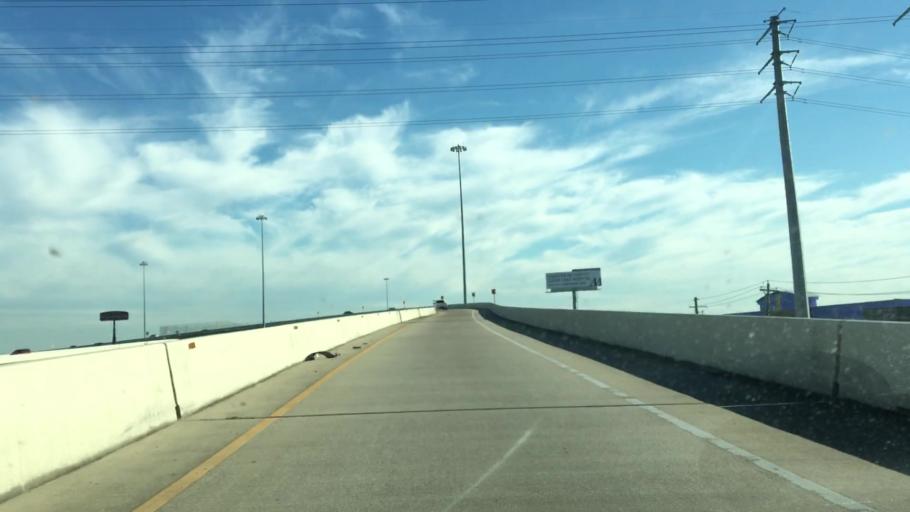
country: US
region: Texas
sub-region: Harris County
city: Webster
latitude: 29.5244
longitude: -95.1275
